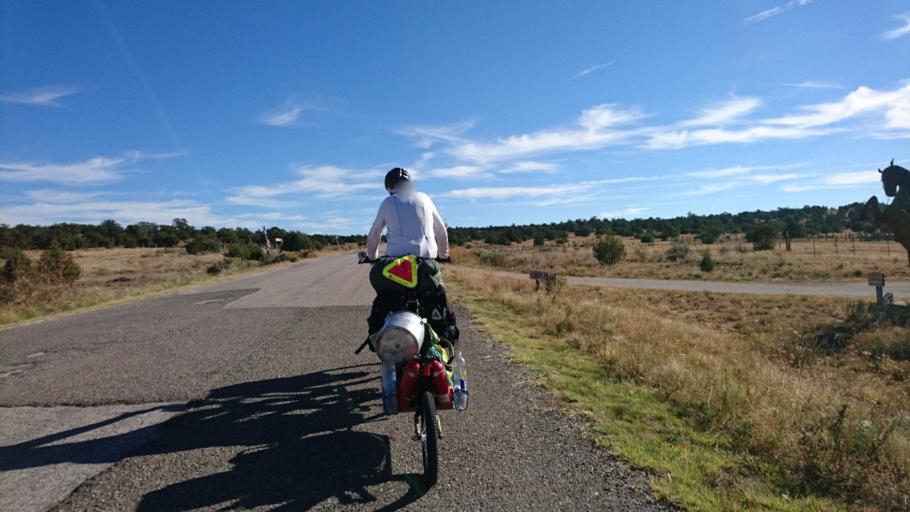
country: US
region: Arizona
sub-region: Mohave County
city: Peach Springs
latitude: 35.5275
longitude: -113.2294
